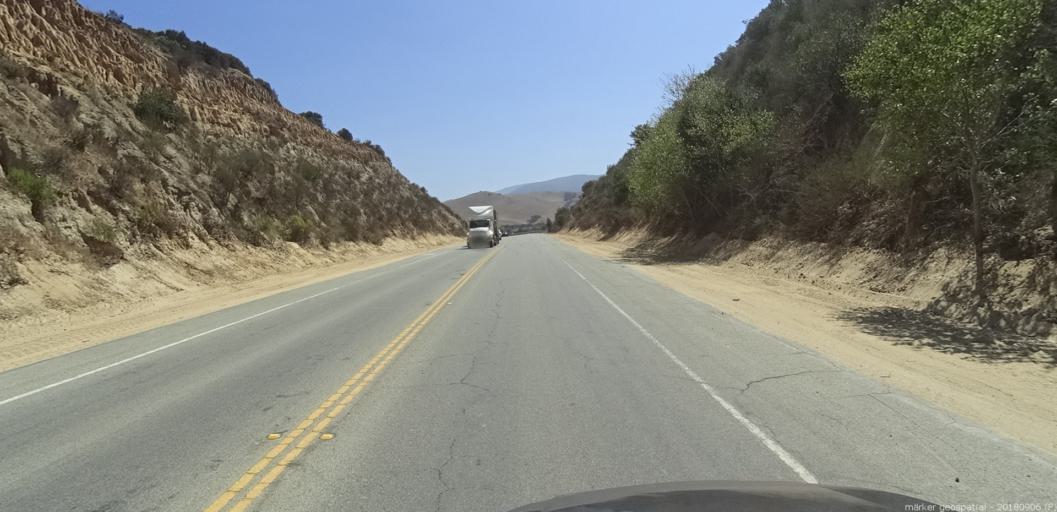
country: US
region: California
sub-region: Monterey County
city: Salinas
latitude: 36.6300
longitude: -121.6918
